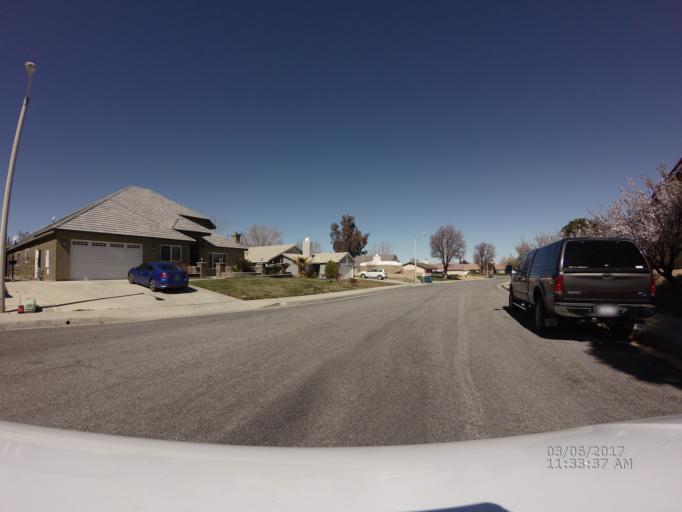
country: US
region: California
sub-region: Los Angeles County
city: Quartz Hill
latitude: 34.6509
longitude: -118.2411
